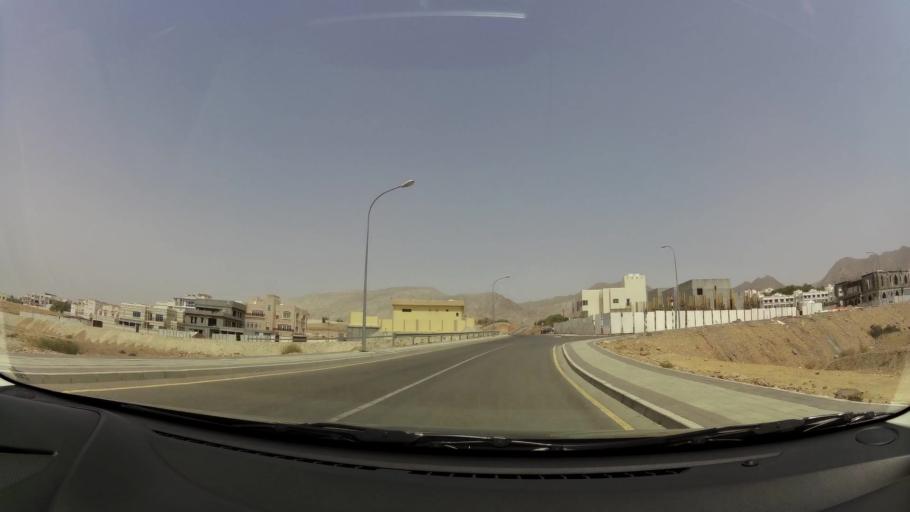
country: OM
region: Muhafazat Masqat
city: Bawshar
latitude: 23.5529
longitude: 58.3929
